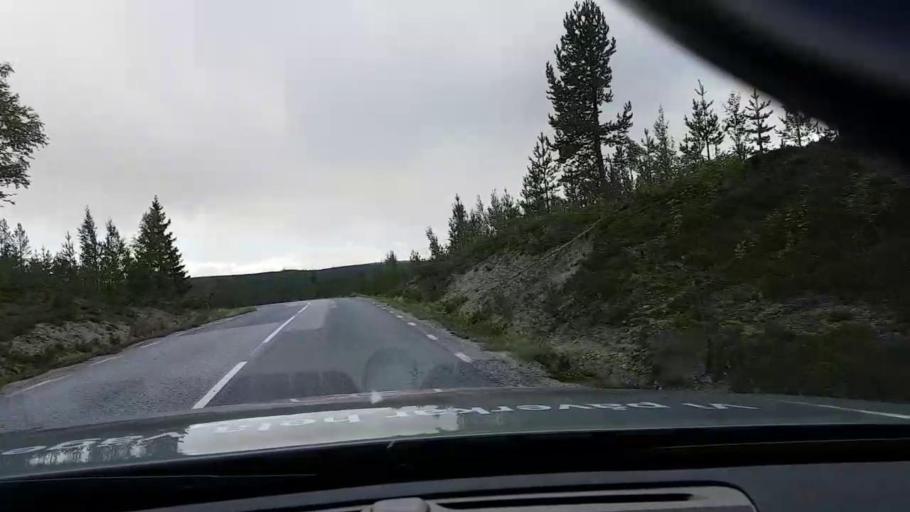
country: SE
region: Vaesterbotten
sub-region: Asele Kommun
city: Asele
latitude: 63.8047
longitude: 17.5470
